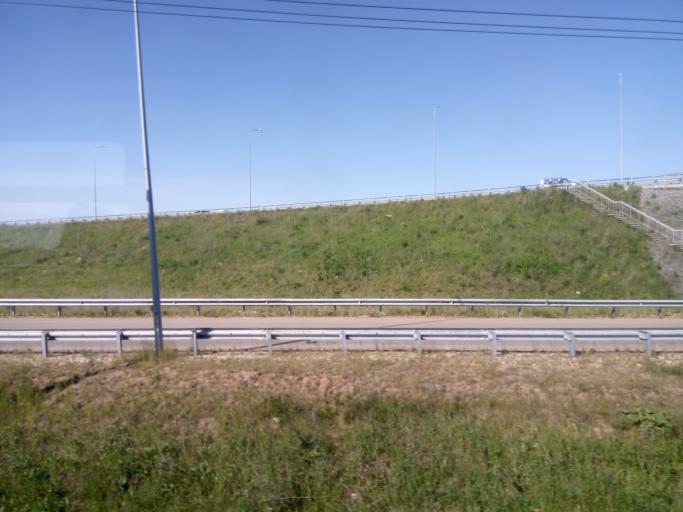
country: RU
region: Tatarstan
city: Stolbishchi
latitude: 55.6667
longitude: 49.2178
